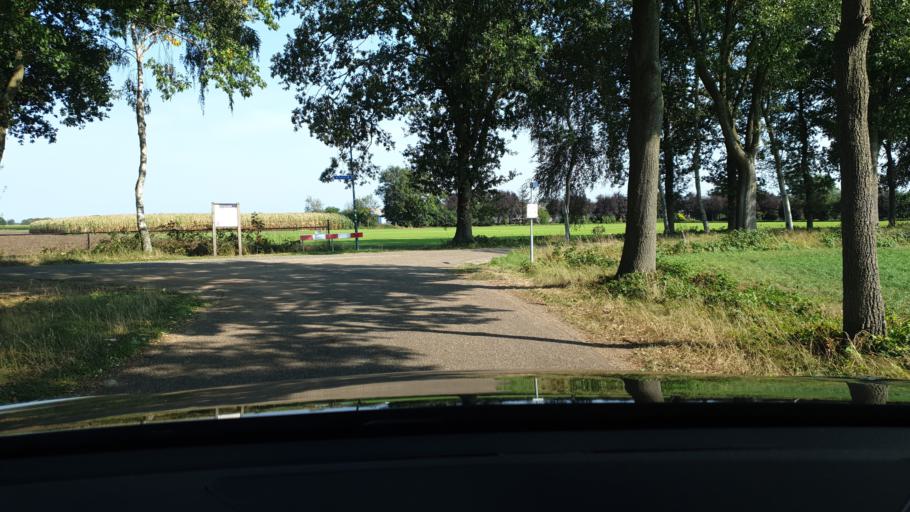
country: NL
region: North Brabant
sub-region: Gemeente Bernheze
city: Loosbroek
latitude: 51.6783
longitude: 5.4709
